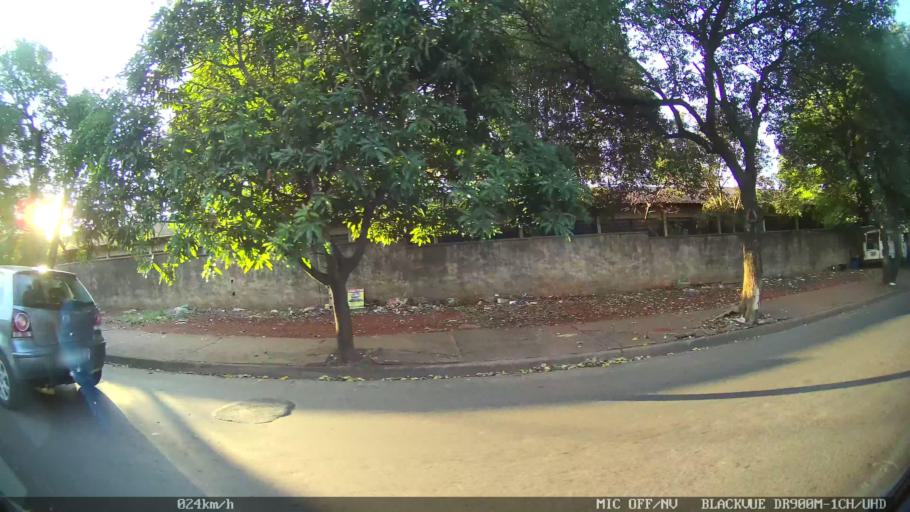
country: BR
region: Sao Paulo
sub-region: Santa Barbara D'Oeste
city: Santa Barbara d'Oeste
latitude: -22.7329
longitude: -47.3807
